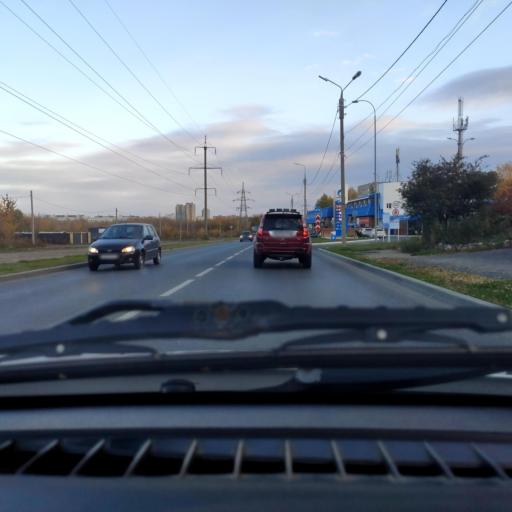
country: RU
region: Samara
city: Tol'yatti
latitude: 53.5222
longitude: 49.3958
